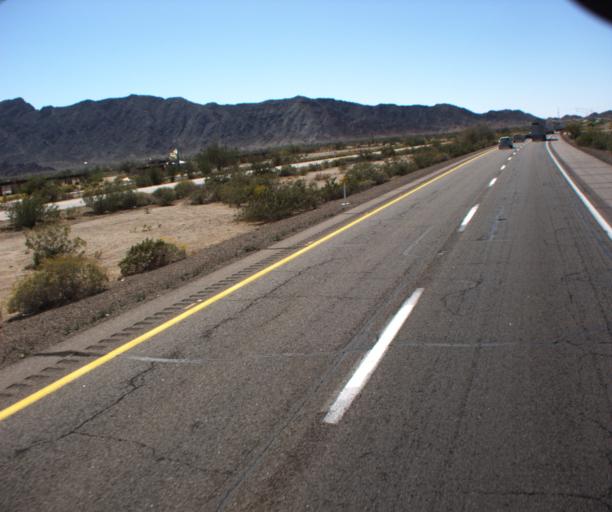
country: US
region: Arizona
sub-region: Yuma County
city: Wellton
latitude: 32.7312
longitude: -113.7154
